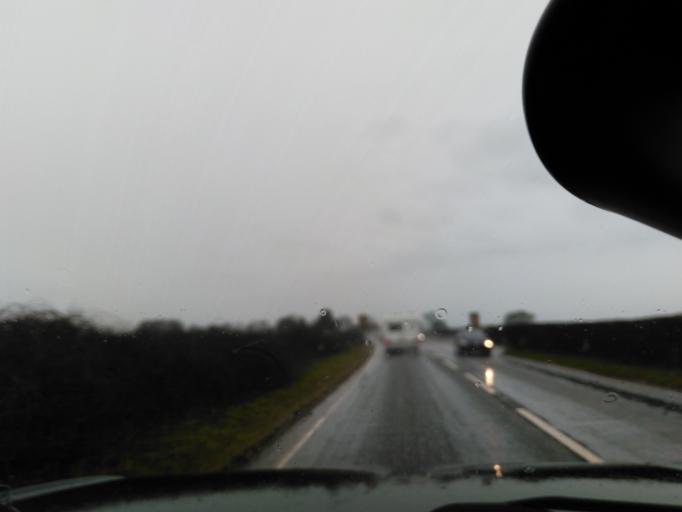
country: GB
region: England
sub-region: Somerset
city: Evercreech
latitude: 51.1918
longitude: -2.4760
